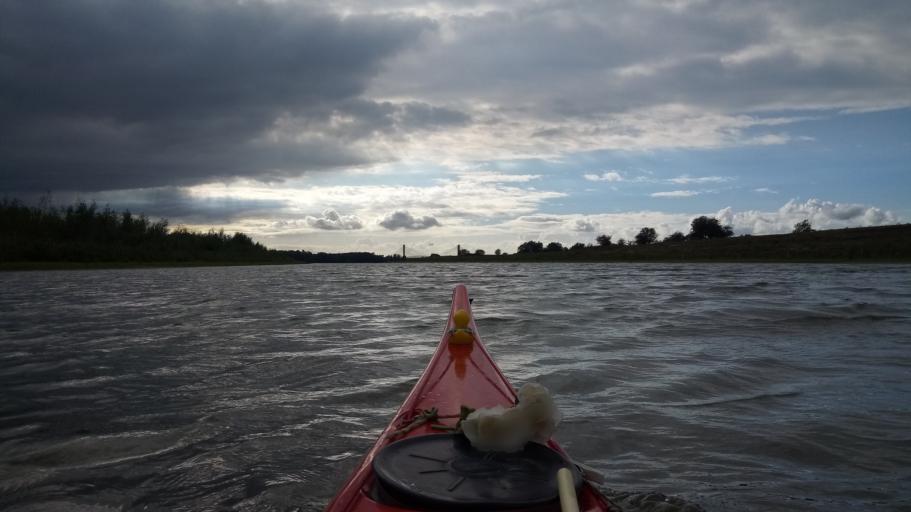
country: NL
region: Gelderland
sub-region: Gemeente Neerijnen
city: Neerijnen
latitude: 51.8186
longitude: 5.3093
